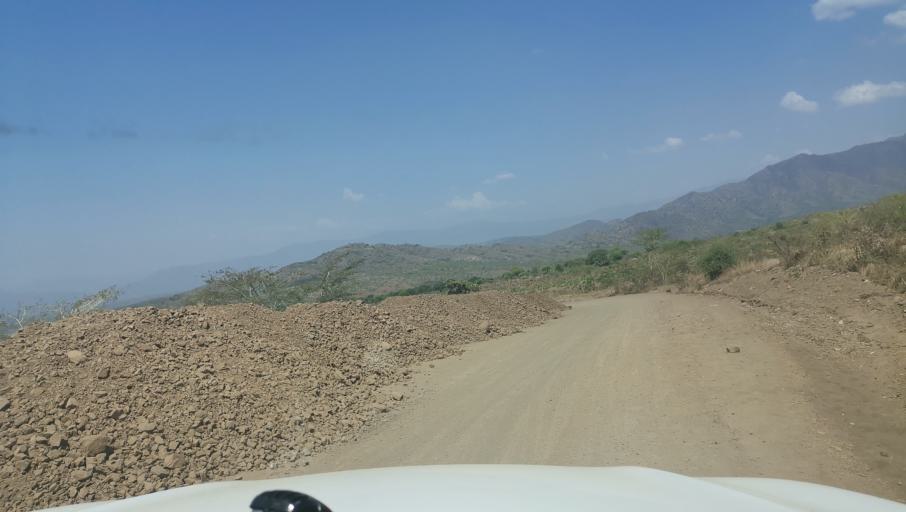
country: ET
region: Southern Nations, Nationalities, and People's Region
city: Arba Minch'
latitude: 6.3342
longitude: 37.3292
